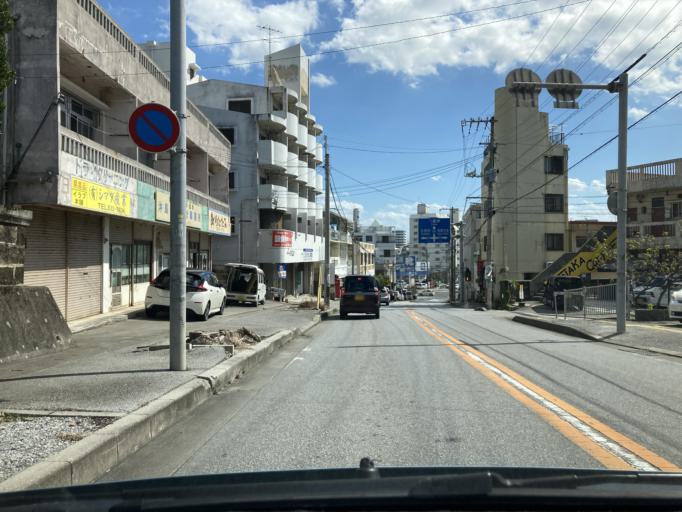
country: JP
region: Okinawa
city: Tomigusuku
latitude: 26.1971
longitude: 127.7038
